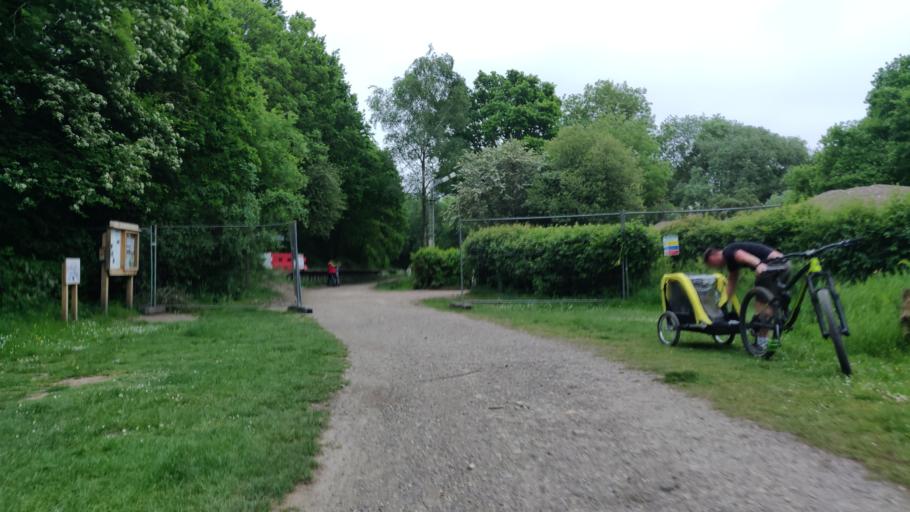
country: GB
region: England
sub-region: West Sussex
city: Partridge Green
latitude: 50.9906
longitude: -0.3144
